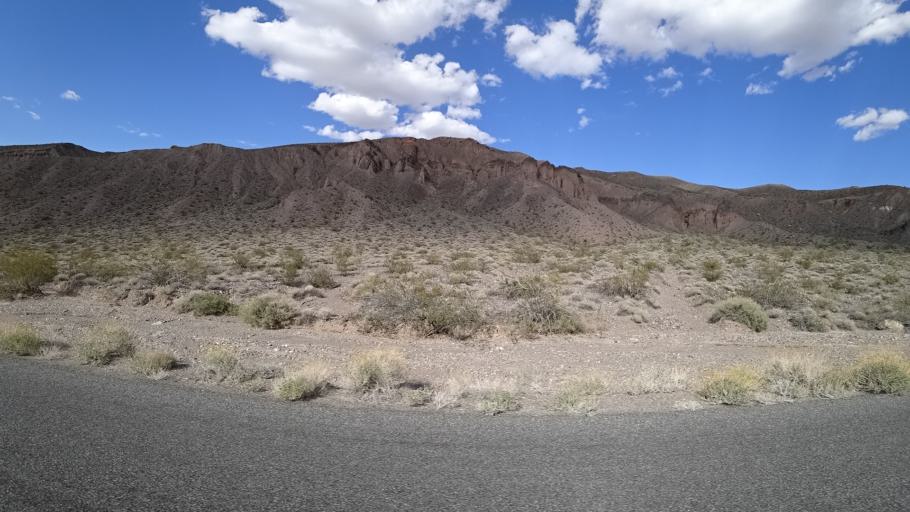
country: US
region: Nevada
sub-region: Nye County
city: Beatty
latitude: 36.4497
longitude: -117.2005
